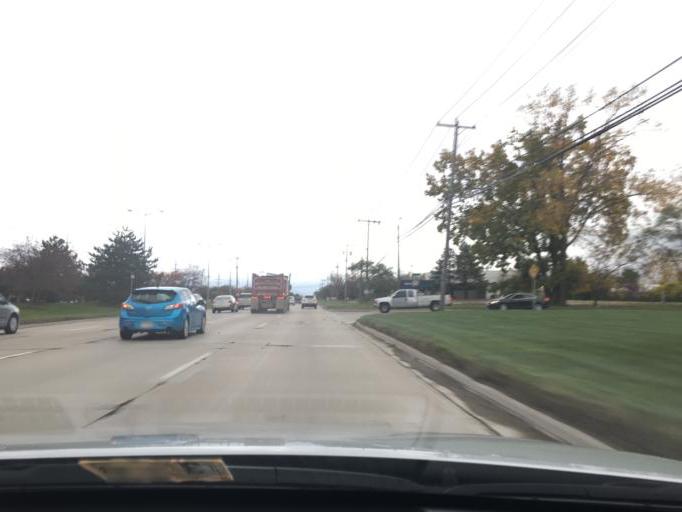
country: US
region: Michigan
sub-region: Macomb County
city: Sterling Heights
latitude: 42.5699
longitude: -83.0491
